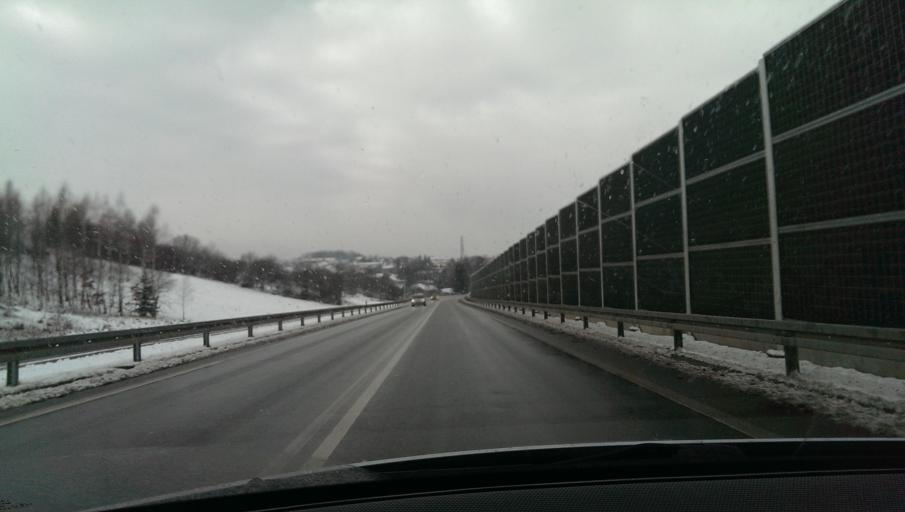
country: PL
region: Subcarpathian Voivodeship
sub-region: Powiat brzozowski
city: Brzozow
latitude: 49.6891
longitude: 22.0349
